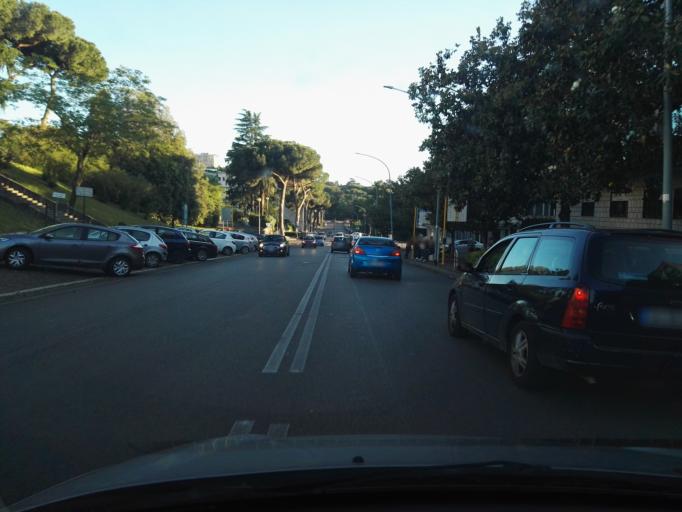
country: IT
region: Latium
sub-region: Citta metropolitana di Roma Capitale
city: Selcetta
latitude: 41.8290
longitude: 12.4740
